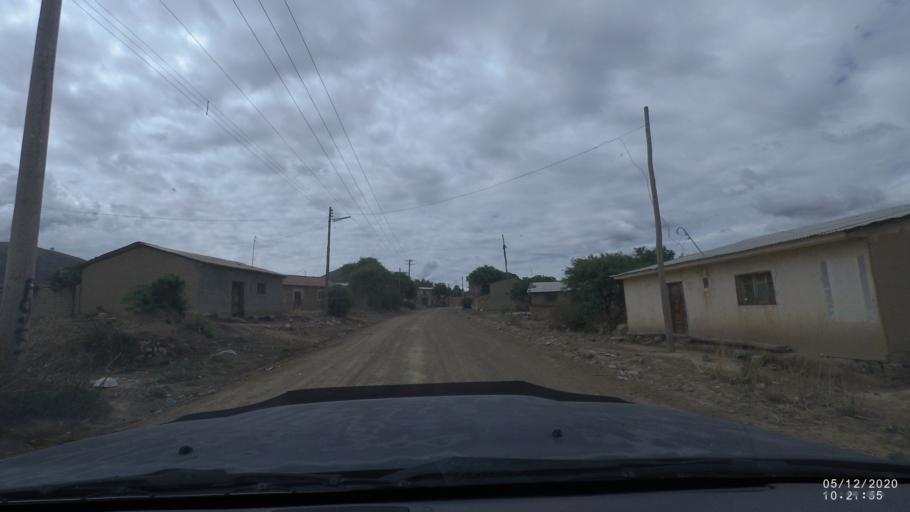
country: BO
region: Cochabamba
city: Sipe Sipe
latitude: -17.4925
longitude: -66.2821
